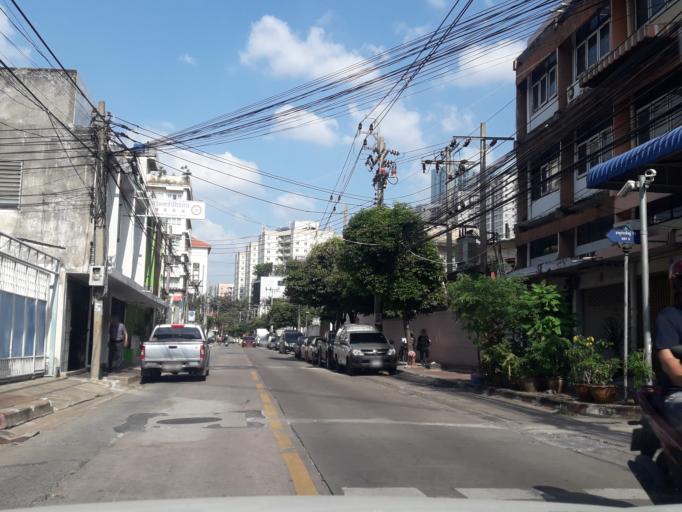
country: TH
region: Bangkok
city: Yan Nawa
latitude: 13.6995
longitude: 100.5333
